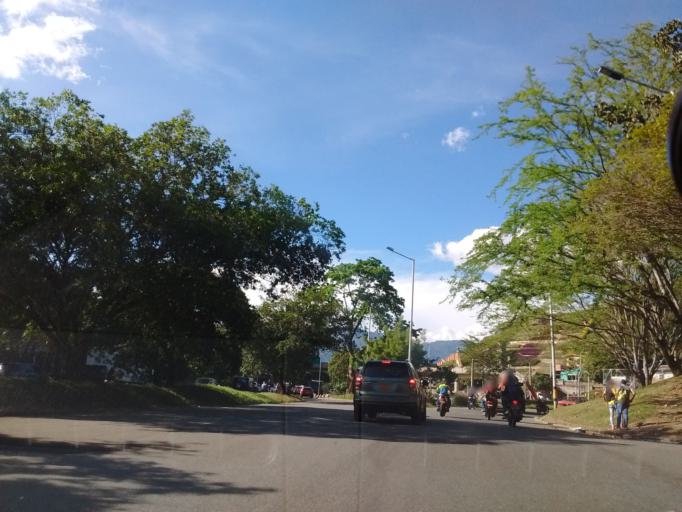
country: CO
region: Antioquia
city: Medellin
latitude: 6.2758
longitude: -75.5691
